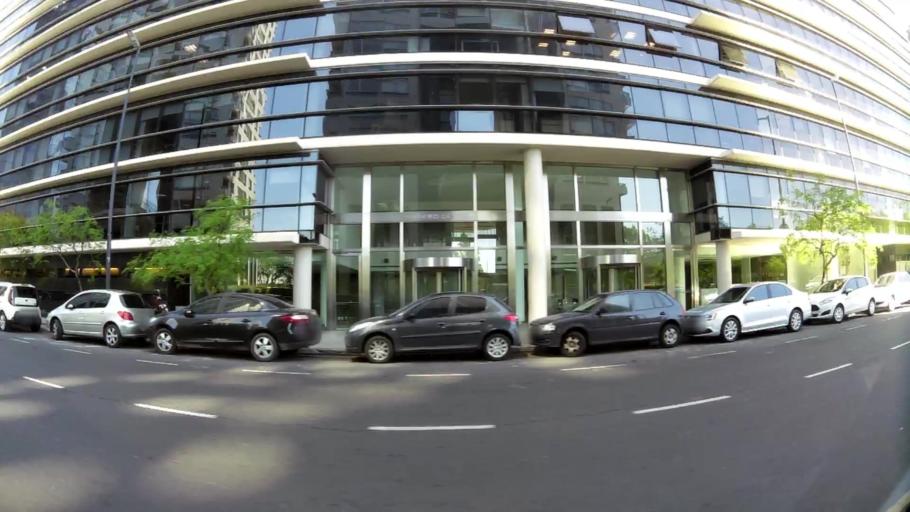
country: AR
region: Buenos Aires F.D.
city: Buenos Aires
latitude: -34.6039
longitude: -58.3634
